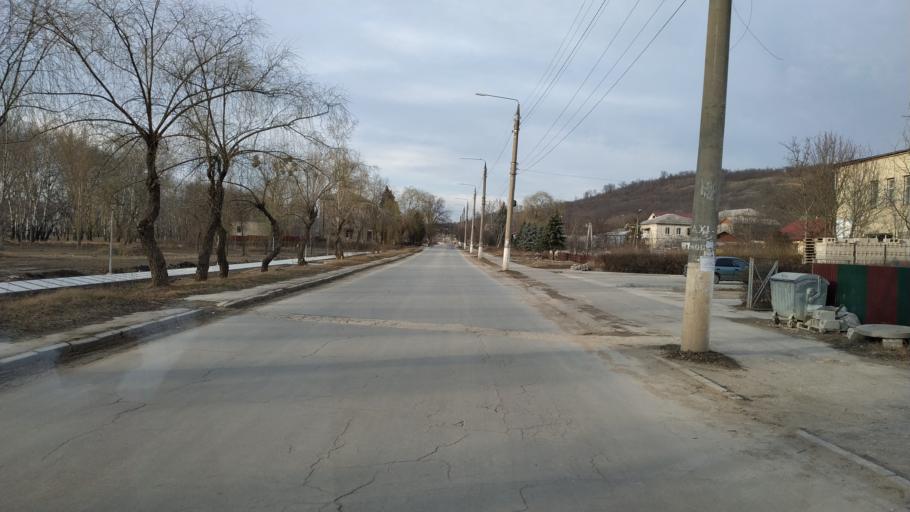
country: MD
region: Nisporeni
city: Nisporeni
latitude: 47.0837
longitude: 28.1825
